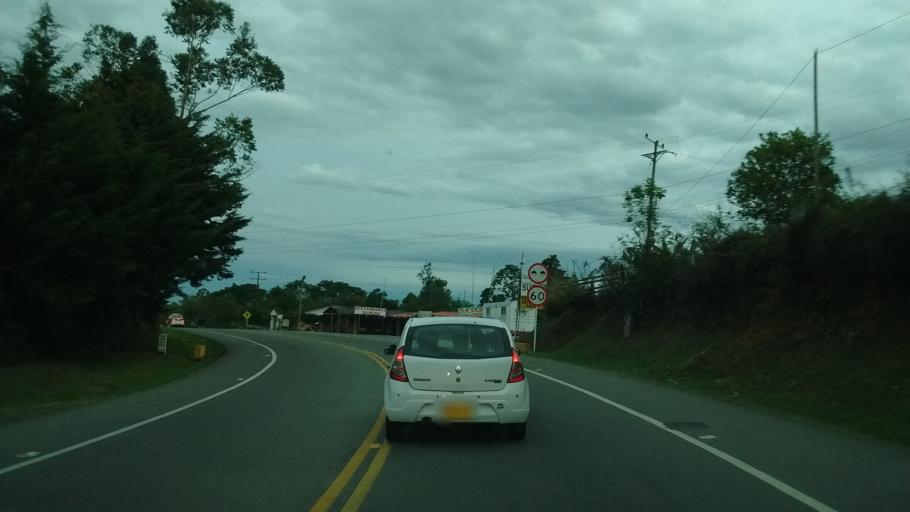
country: CO
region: Cauca
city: Cajibio
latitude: 2.6856
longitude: -76.5272
